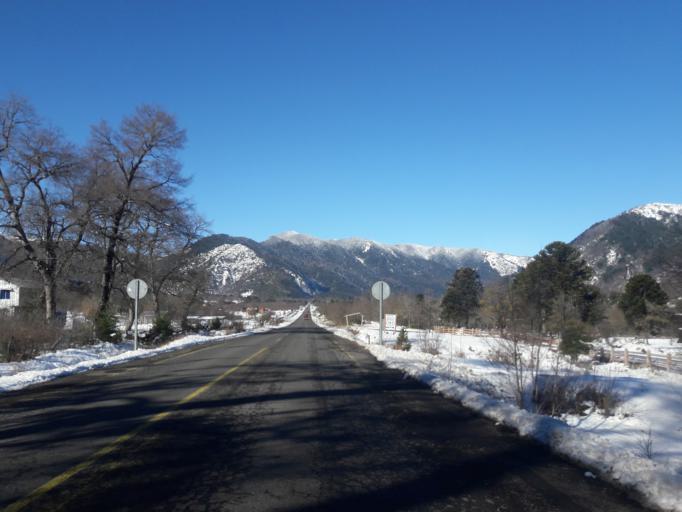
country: CL
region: Araucania
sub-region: Provincia de Cautin
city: Vilcun
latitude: -38.4732
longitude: -71.5591
